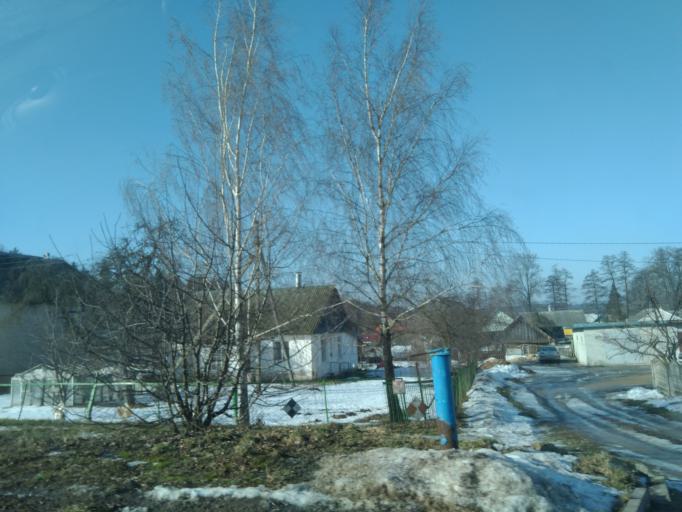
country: BY
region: Minsk
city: Nyasvizh
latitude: 53.2070
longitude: 26.6612
